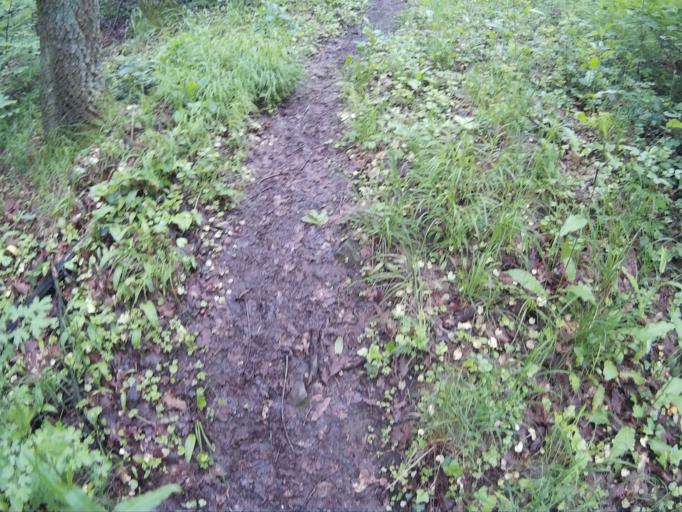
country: HU
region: Veszprem
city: Sumeg
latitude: 46.9042
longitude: 17.2648
